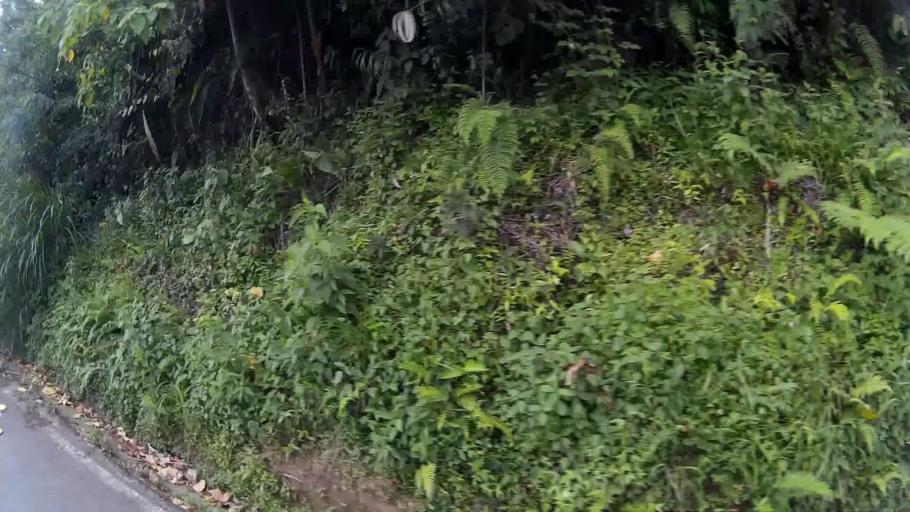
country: CO
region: Risaralda
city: Marsella
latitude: 4.9012
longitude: -75.7324
